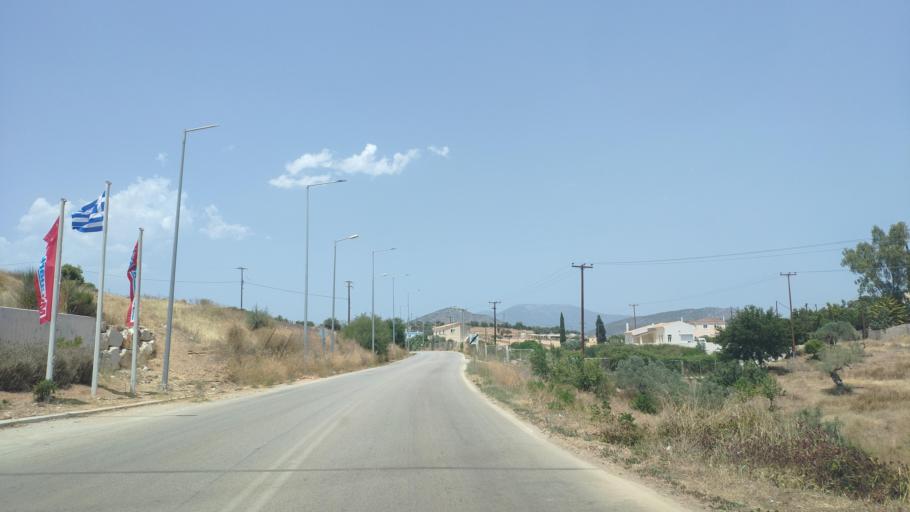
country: GR
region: Peloponnese
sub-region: Nomos Argolidos
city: Kranidi
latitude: 37.3615
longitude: 23.1626
